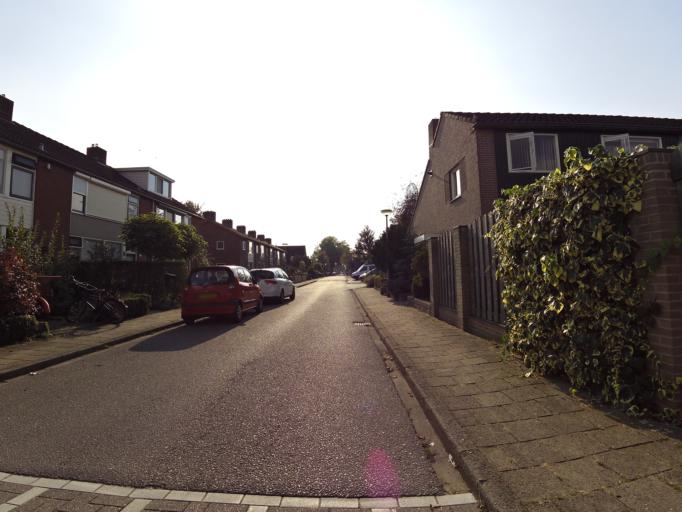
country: NL
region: Gelderland
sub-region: Gemeente Aalten
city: Aalten
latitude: 51.9205
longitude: 6.5886
